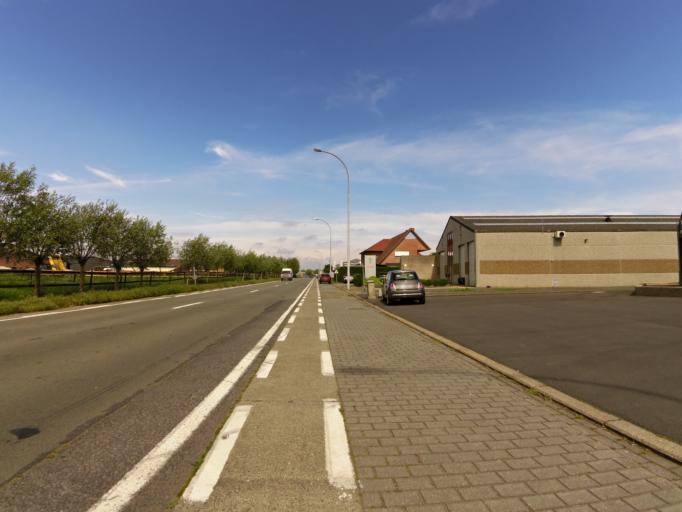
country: BE
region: Flanders
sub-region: Provincie West-Vlaanderen
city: Ichtegem
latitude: 51.0993
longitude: 3.0206
